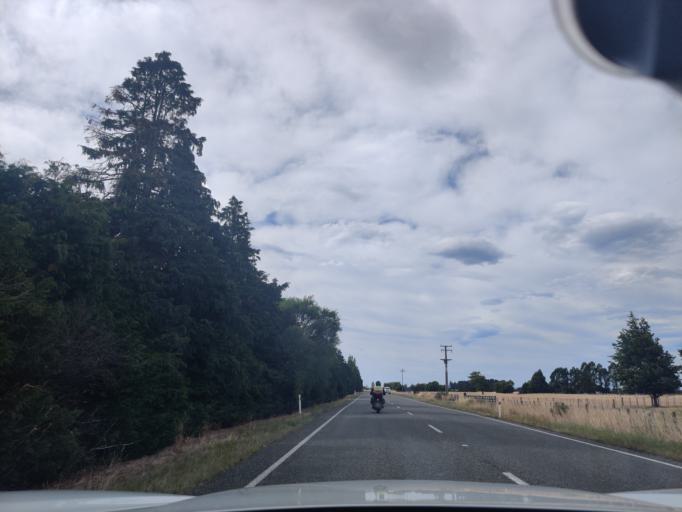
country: NZ
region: Wellington
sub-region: Masterton District
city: Masterton
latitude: -40.8675
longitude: 175.6460
